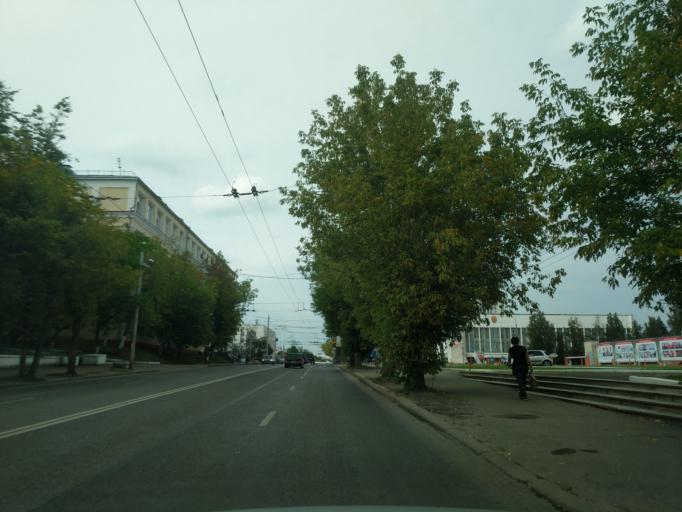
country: RU
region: Kirov
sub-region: Kirovo-Chepetskiy Rayon
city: Kirov
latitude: 58.5928
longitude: 49.6688
